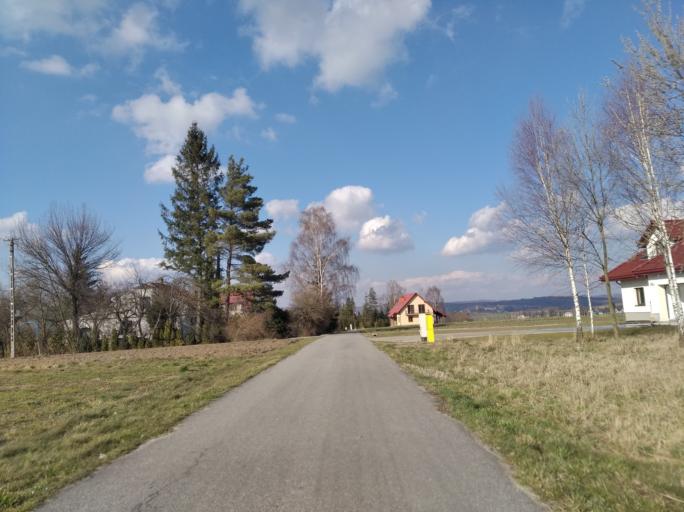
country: PL
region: Subcarpathian Voivodeship
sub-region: Powiat strzyzowski
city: Wysoka Strzyzowska
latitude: 49.8504
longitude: 21.7098
